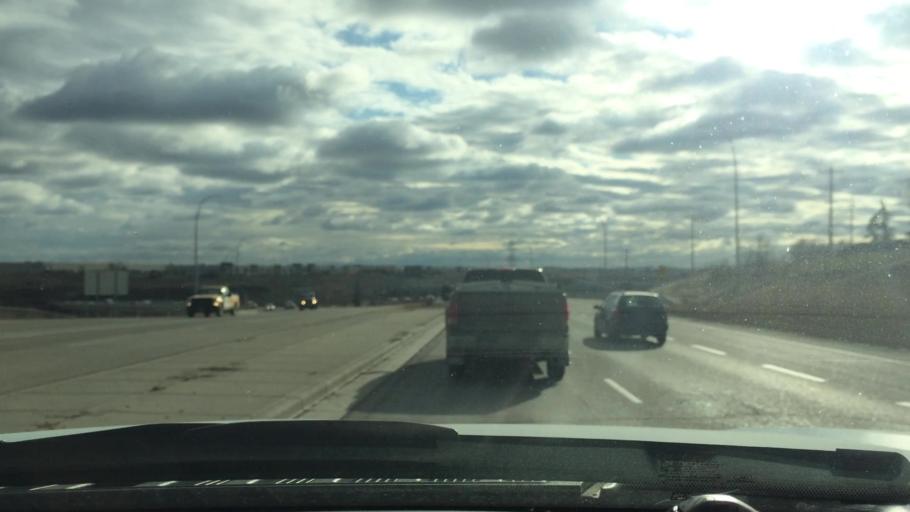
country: CA
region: Alberta
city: Calgary
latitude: 51.1271
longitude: -114.0518
